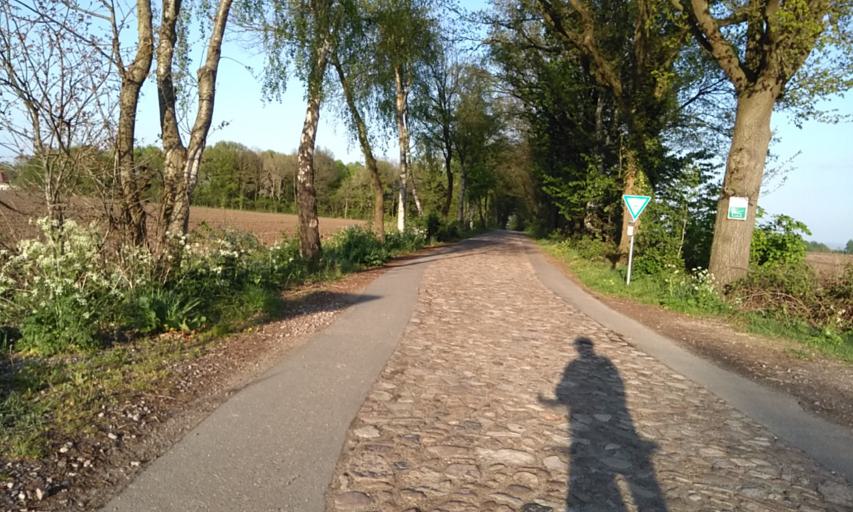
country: DE
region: Lower Saxony
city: Dollern
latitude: 53.5330
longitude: 9.5523
